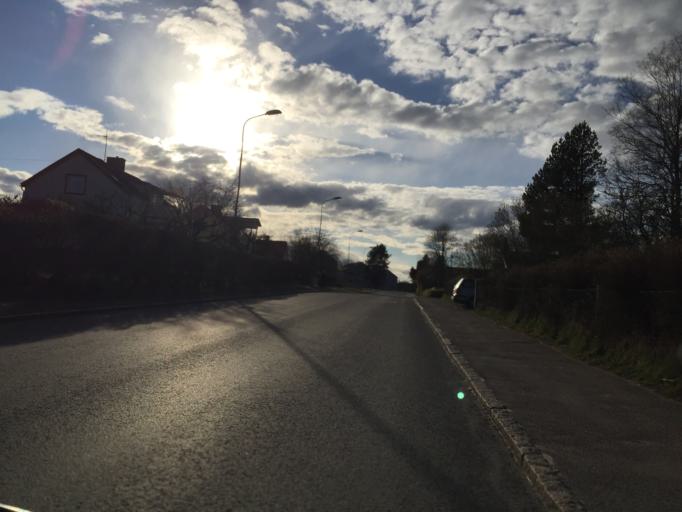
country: SE
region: Dalarna
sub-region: Ludvika Kommun
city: Ludvika
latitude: 60.1253
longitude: 15.1881
